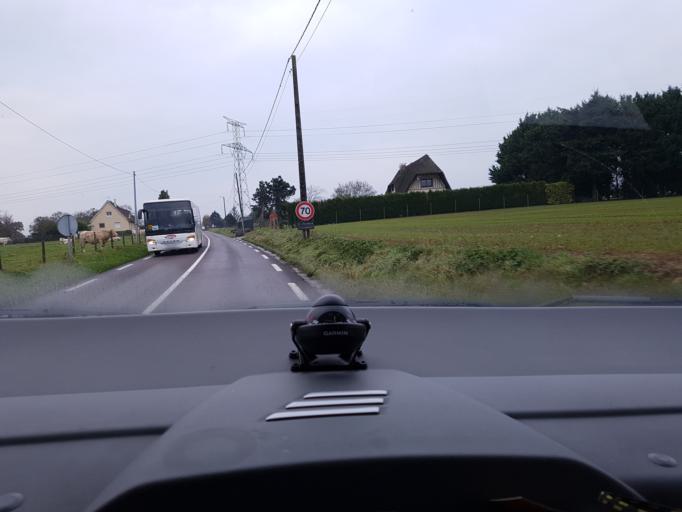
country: FR
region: Haute-Normandie
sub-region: Departement de la Seine-Maritime
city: Roumare
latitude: 49.4995
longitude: 0.9787
